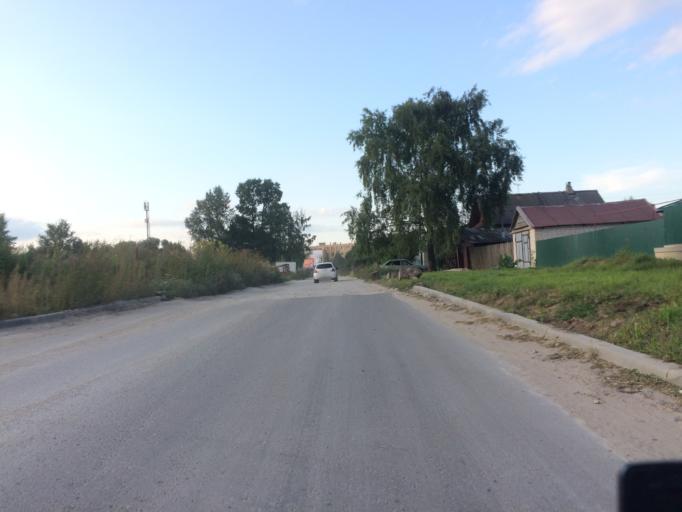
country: RU
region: Mariy-El
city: Medvedevo
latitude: 56.6514
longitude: 47.8383
